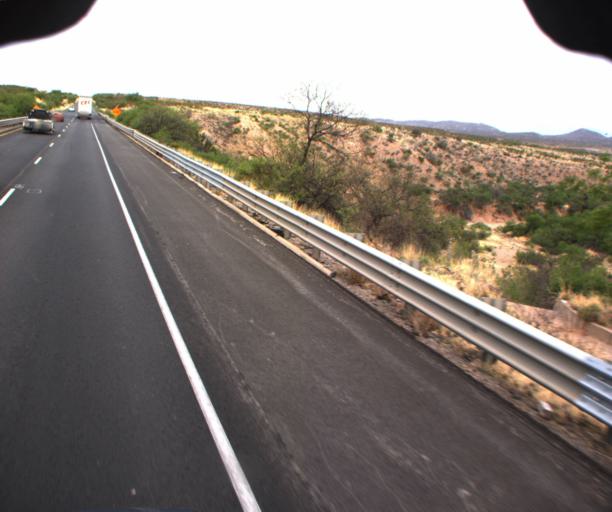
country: US
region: Arizona
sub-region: Pima County
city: Vail
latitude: 31.9942
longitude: -110.6103
